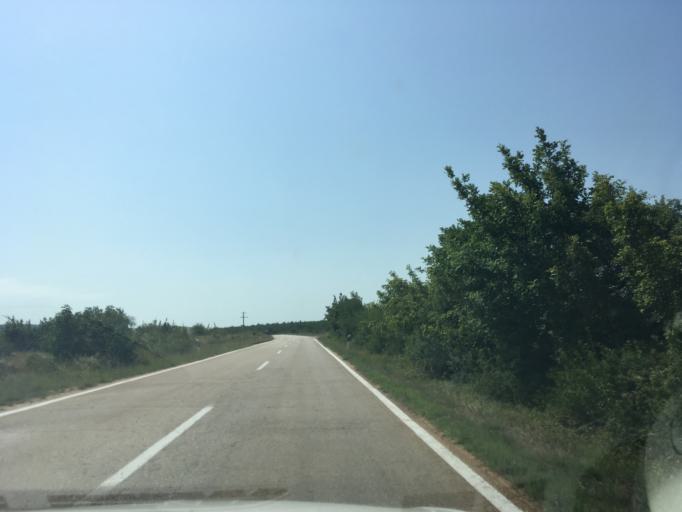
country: HR
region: Zadarska
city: Benkovac
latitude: 43.9649
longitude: 15.7433
